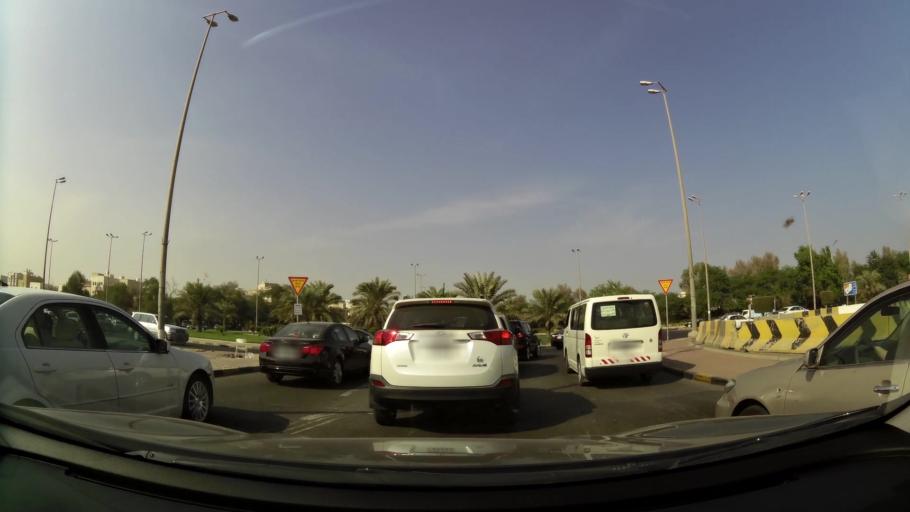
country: KW
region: Mubarak al Kabir
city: Mubarak al Kabir
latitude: 29.1745
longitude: 48.0845
